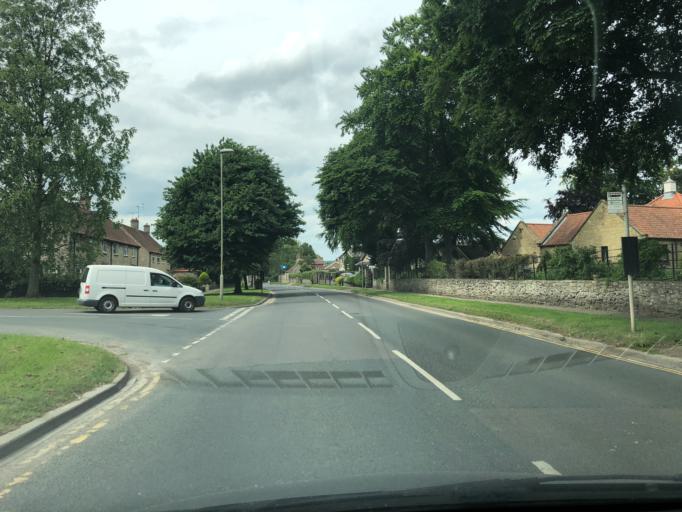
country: GB
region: England
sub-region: North Yorkshire
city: Pickering
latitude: 54.2481
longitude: -0.7899
